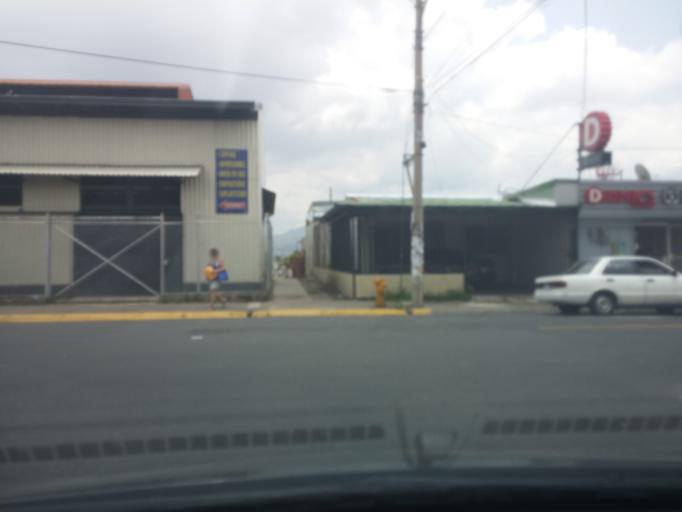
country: CR
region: Heredia
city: Llorente
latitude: 9.9881
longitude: -84.1509
